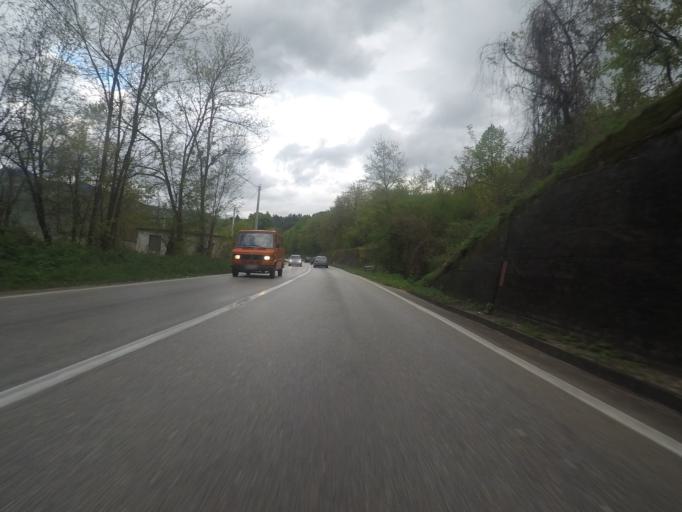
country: BA
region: Federation of Bosnia and Herzegovina
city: Konjic
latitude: 43.6854
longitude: 17.8787
